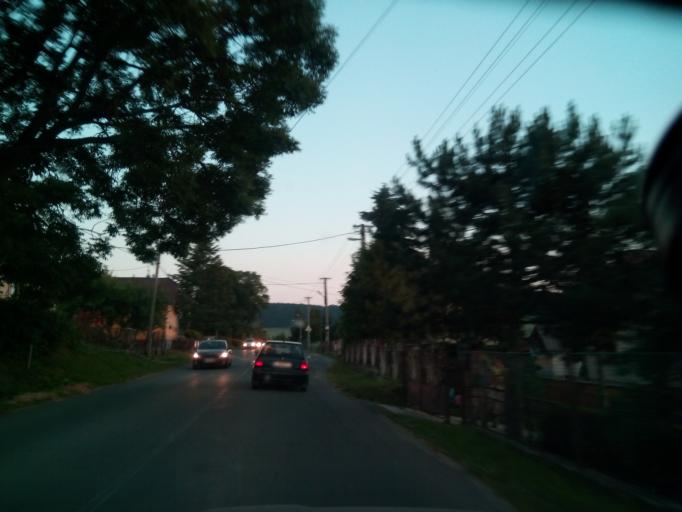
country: SK
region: Presovsky
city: Lubica
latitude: 49.0617
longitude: 20.4309
